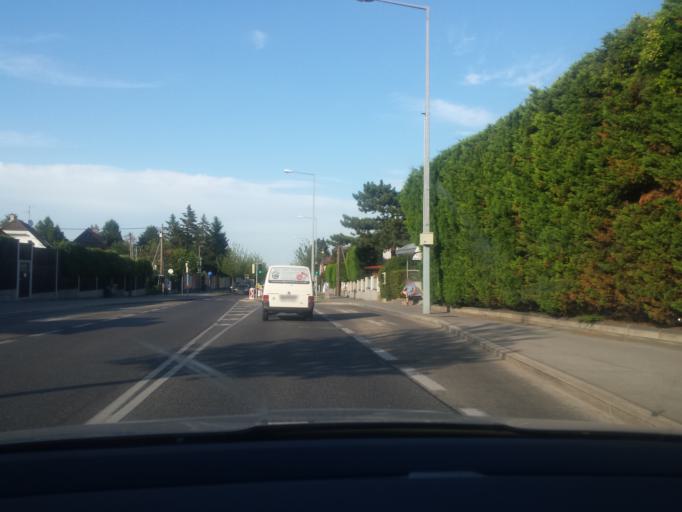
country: AT
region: Lower Austria
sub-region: Politischer Bezirk Wien-Umgebung
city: Leopoldsdorf
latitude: 48.1579
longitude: 16.3997
